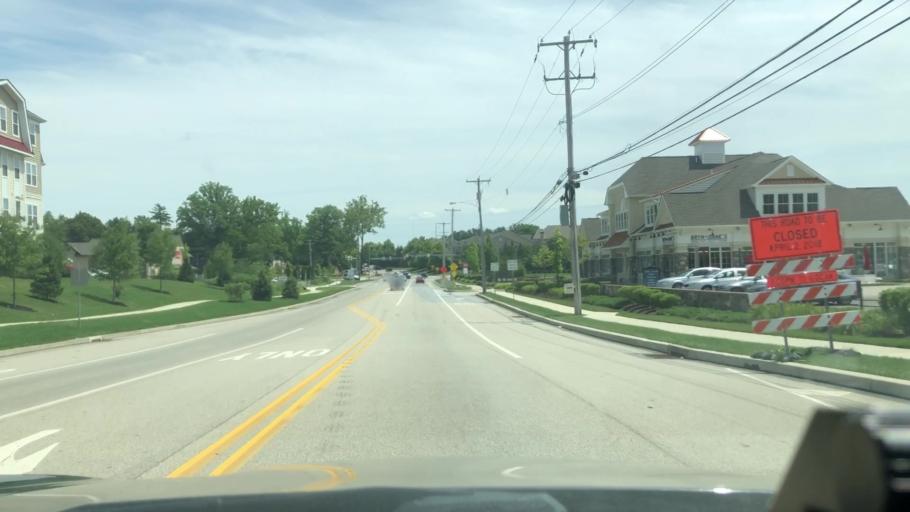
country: US
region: Pennsylvania
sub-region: Montgomery County
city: Plymouth Meeting
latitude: 40.1096
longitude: -75.2752
